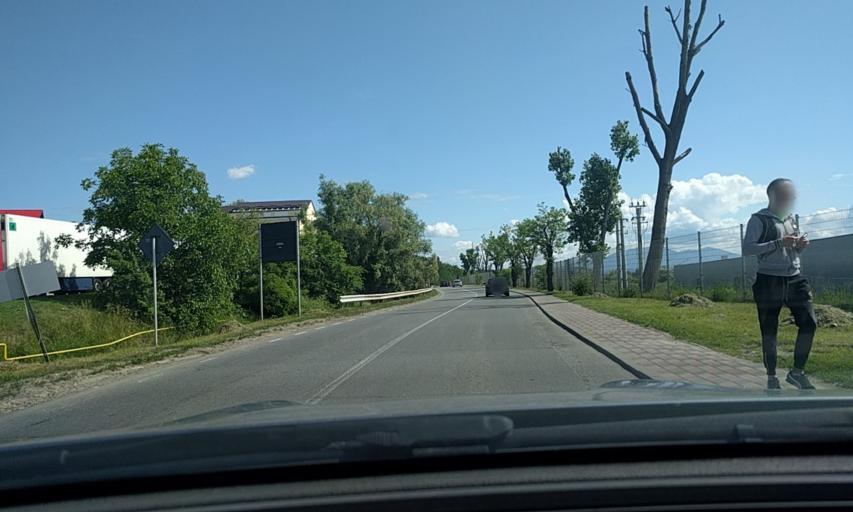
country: RO
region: Bistrita-Nasaud
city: Bistrita
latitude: 47.1384
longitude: 24.4801
